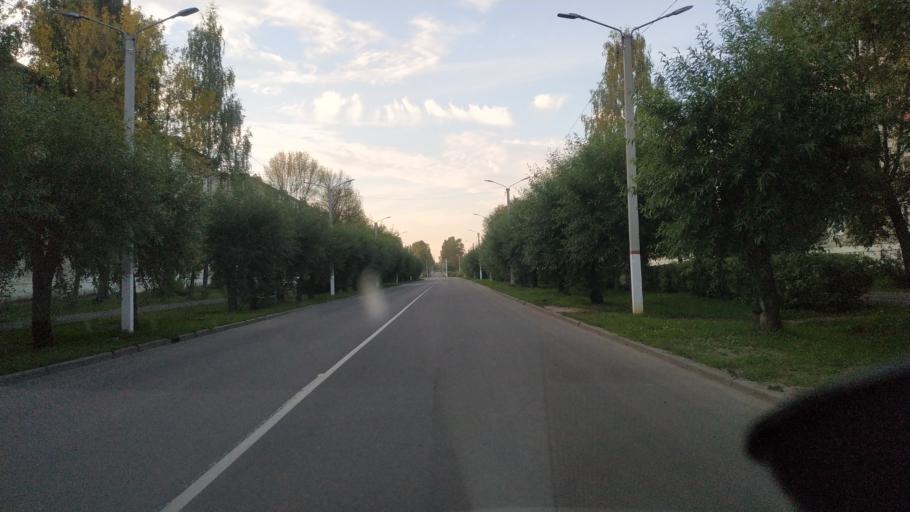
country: RU
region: Moskovskaya
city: Roshal'
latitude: 55.6643
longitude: 39.8526
